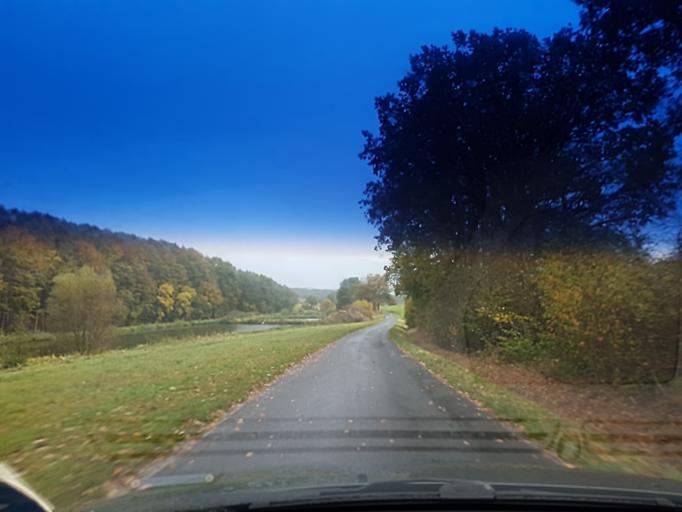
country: DE
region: Bavaria
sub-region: Regierungsbezirk Mittelfranken
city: Wachenroth
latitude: 49.7638
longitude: 10.6698
